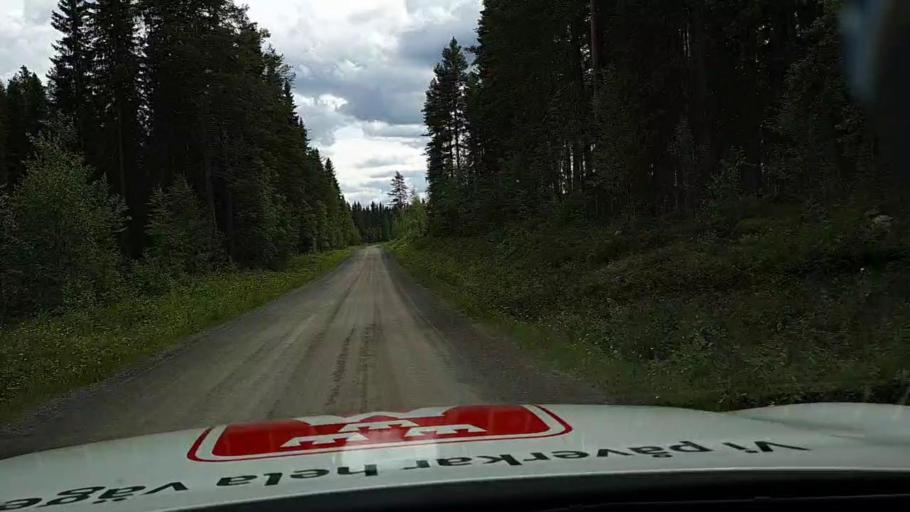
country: SE
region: Jaemtland
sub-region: Braecke Kommun
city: Braecke
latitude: 63.2746
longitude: 15.3758
